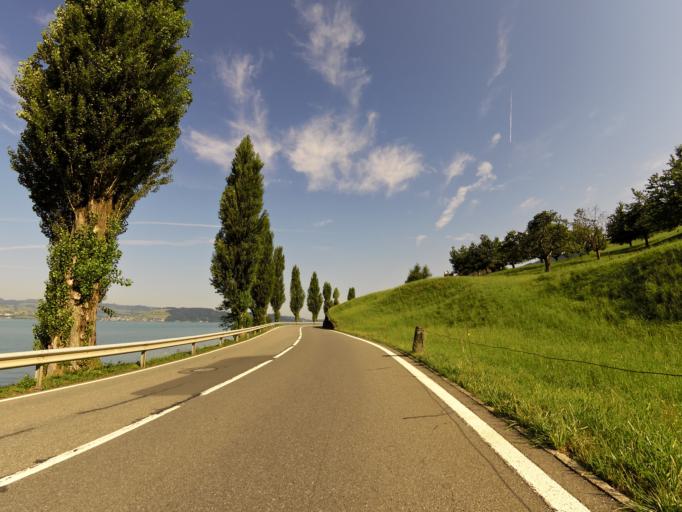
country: CH
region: Schwyz
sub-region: Bezirk Schwyz
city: Arth
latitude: 47.0794
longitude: 8.5248
